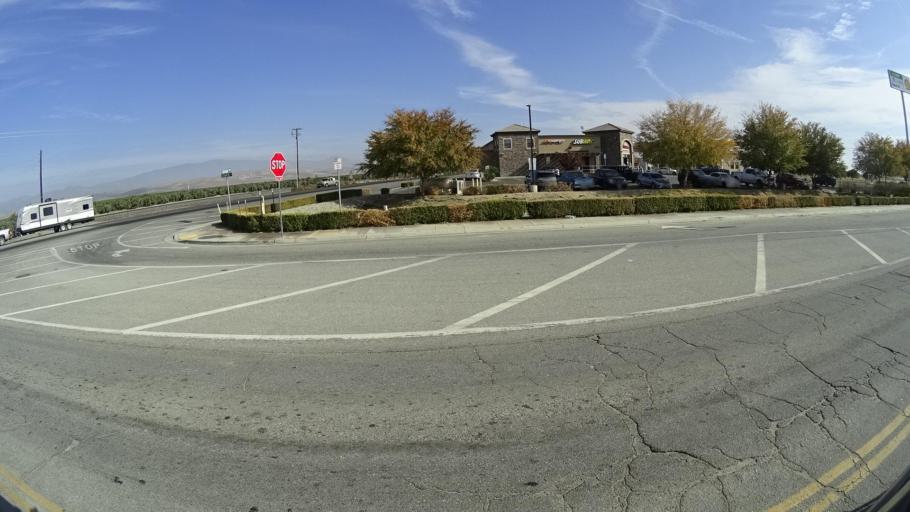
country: US
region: California
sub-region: Kern County
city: Lamont
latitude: 35.3409
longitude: -118.8433
